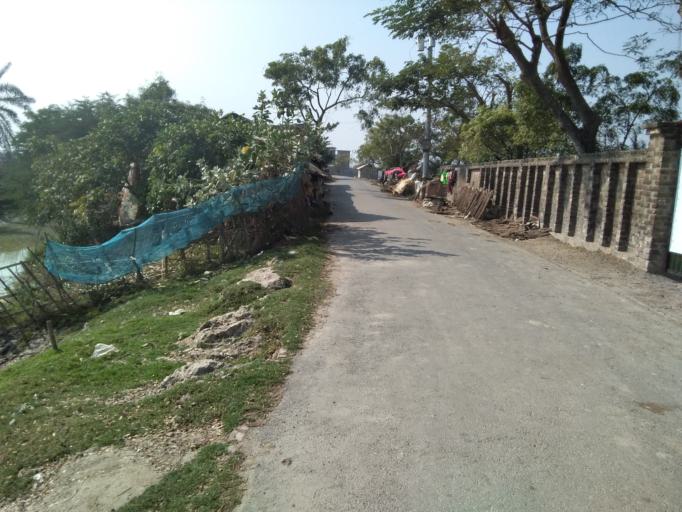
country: BD
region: Khulna
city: Satkhira
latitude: 22.6336
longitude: 89.0180
